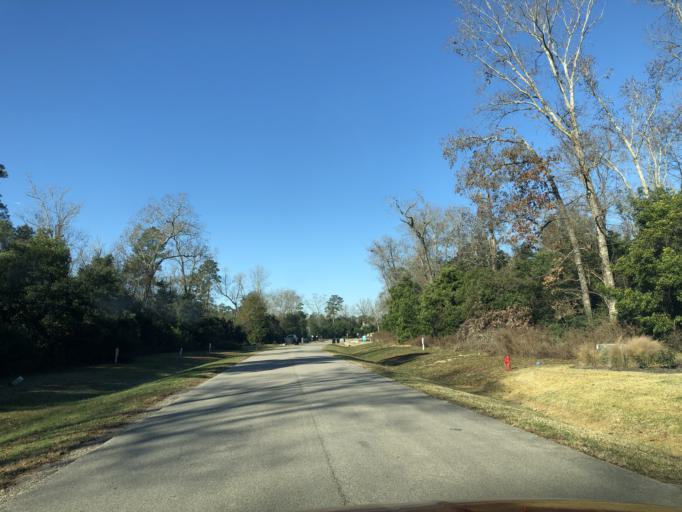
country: US
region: Texas
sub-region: Montgomery County
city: Porter Heights
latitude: 30.0708
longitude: -95.3321
